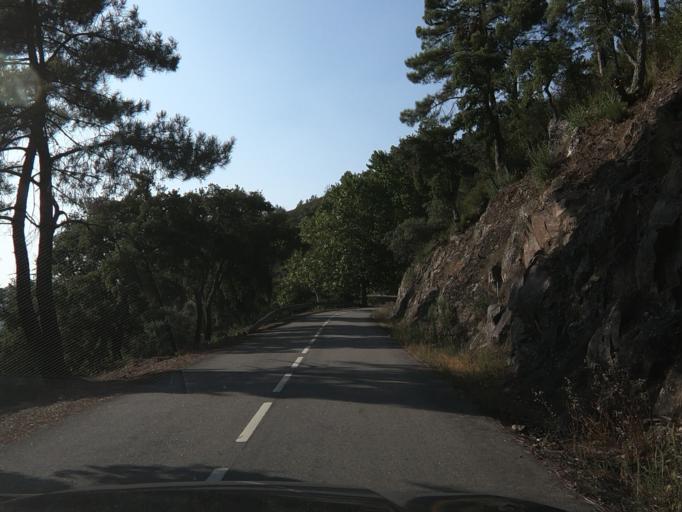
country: PT
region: Vila Real
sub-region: Sabrosa
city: Vilela
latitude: 41.2046
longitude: -7.6239
